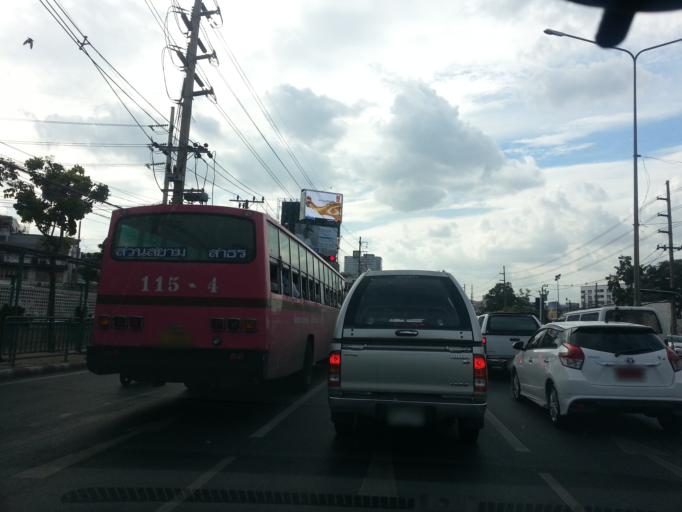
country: TH
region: Bangkok
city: Khlong Toei
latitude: 13.7205
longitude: 100.5582
